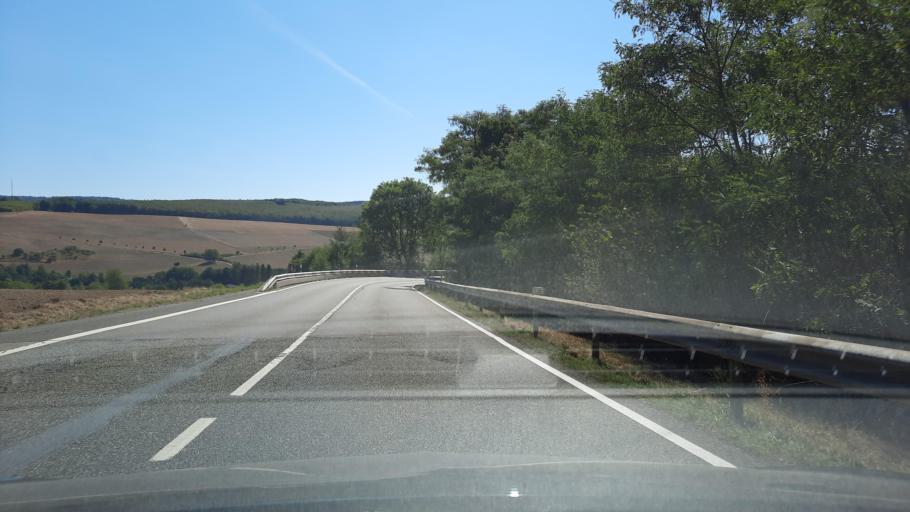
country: DE
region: Rheinland-Pfalz
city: Zerf
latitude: 49.6005
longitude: 6.6763
